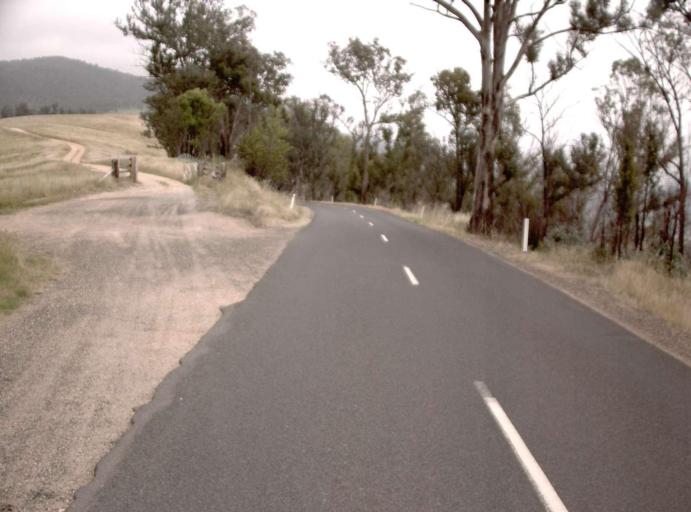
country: AU
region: Victoria
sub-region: Wellington
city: Heyfield
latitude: -37.8270
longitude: 146.6775
